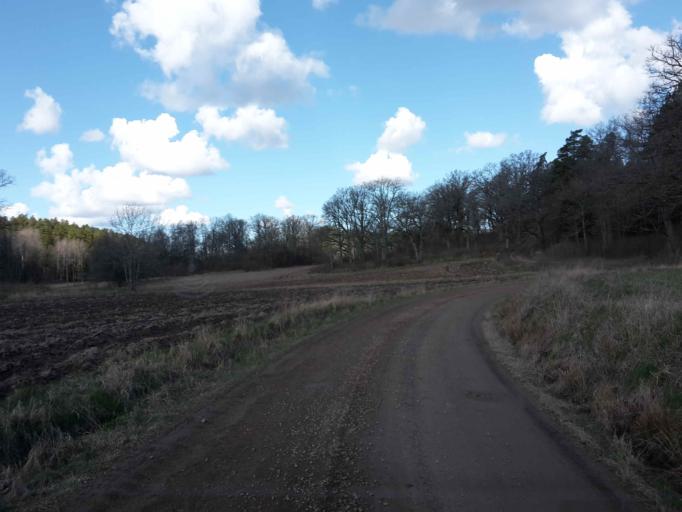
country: SE
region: OEstergoetland
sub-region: Linkopings Kommun
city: Sturefors
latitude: 58.3057
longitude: 15.8556
